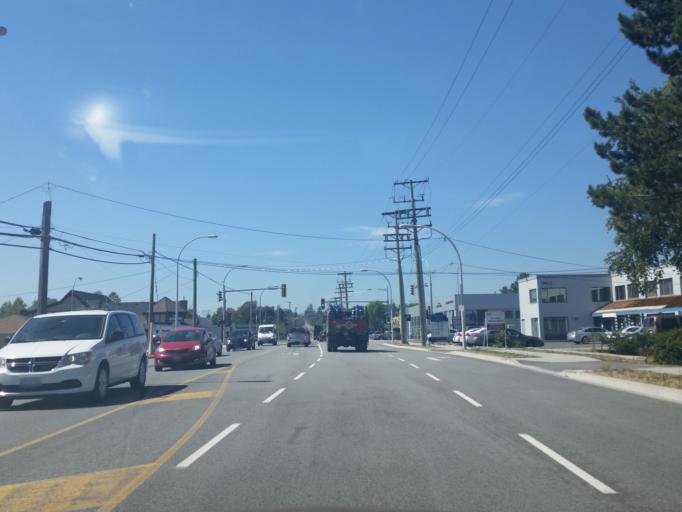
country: CA
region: British Columbia
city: Langley
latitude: 49.1044
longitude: -122.6785
